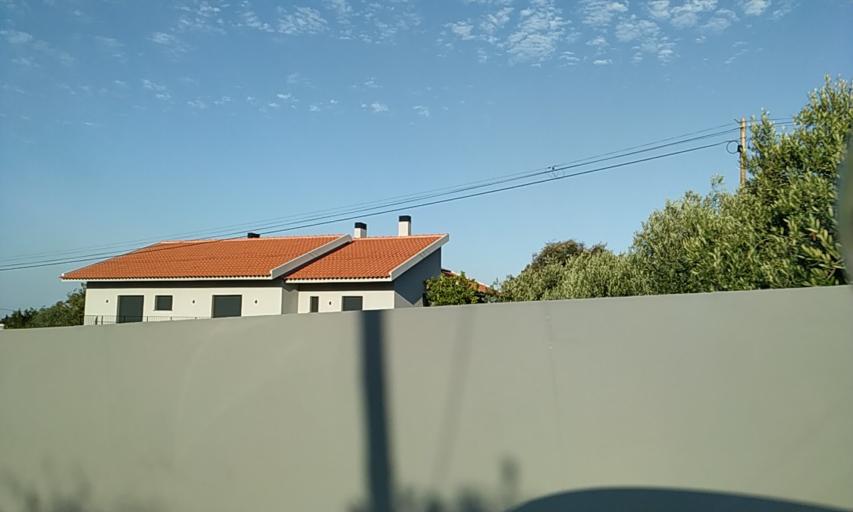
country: PT
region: Santarem
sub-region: Alcanena
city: Alcanena
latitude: 39.4475
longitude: -8.6229
